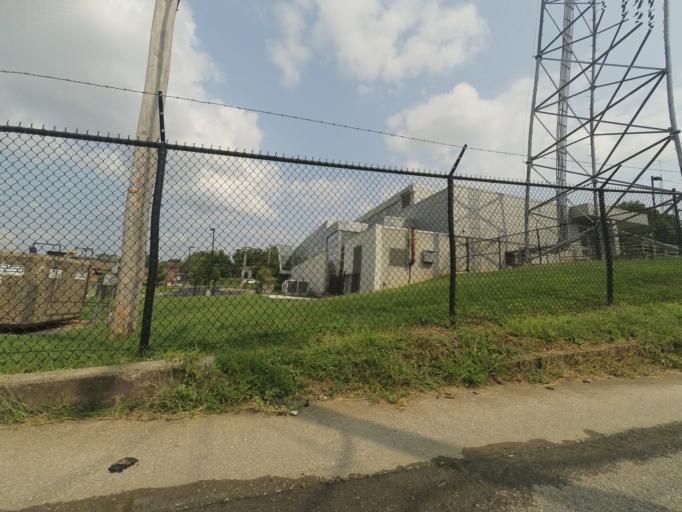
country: US
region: West Virginia
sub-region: Cabell County
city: Huntington
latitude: 38.4063
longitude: -82.4071
